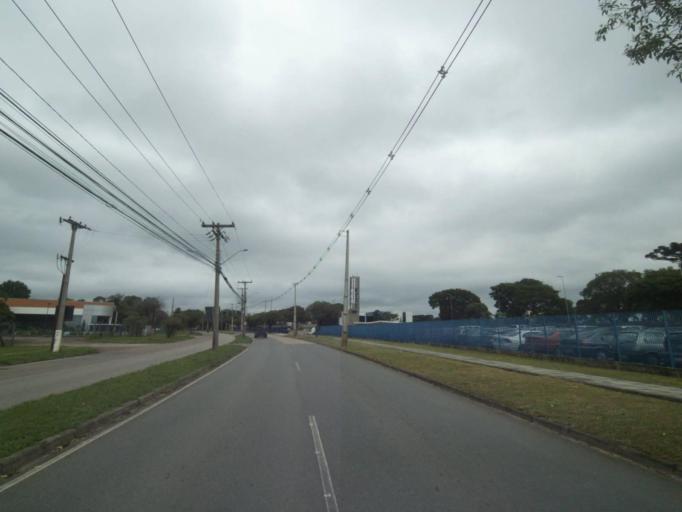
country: BR
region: Parana
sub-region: Sao Jose Dos Pinhais
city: Sao Jose dos Pinhais
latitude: -25.5520
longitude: -49.3114
